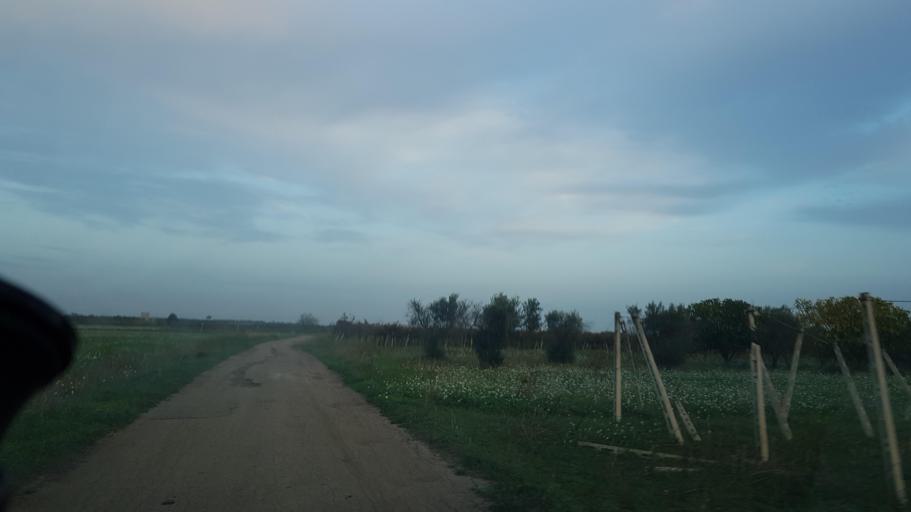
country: IT
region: Apulia
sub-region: Provincia di Brindisi
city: San Donaci
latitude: 40.4260
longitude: 17.9231
